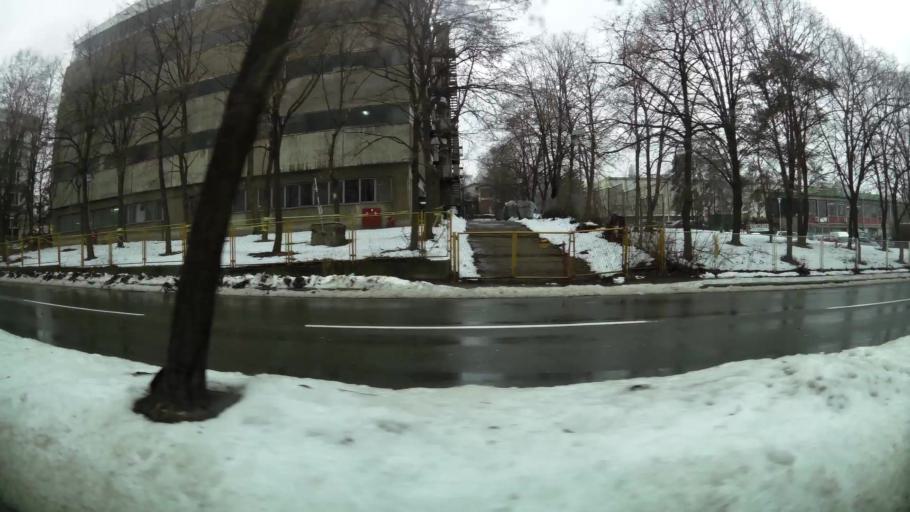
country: RS
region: Central Serbia
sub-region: Belgrade
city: Vozdovac
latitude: 44.7640
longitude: 20.4888
